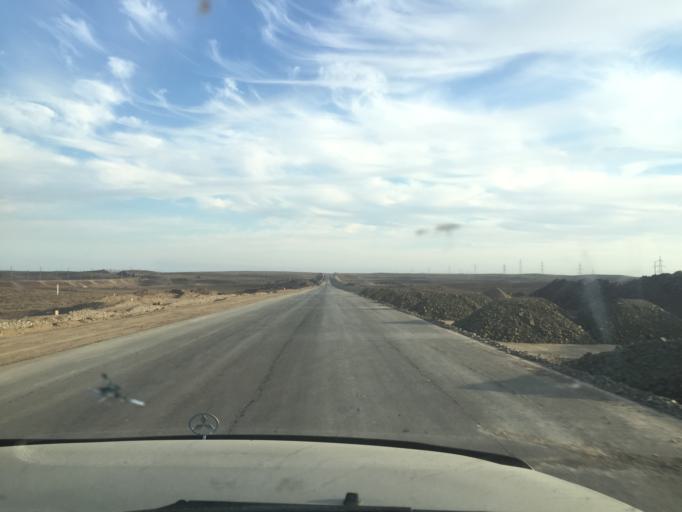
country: KZ
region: Zhambyl
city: Mynaral
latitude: 45.2781
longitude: 73.7810
